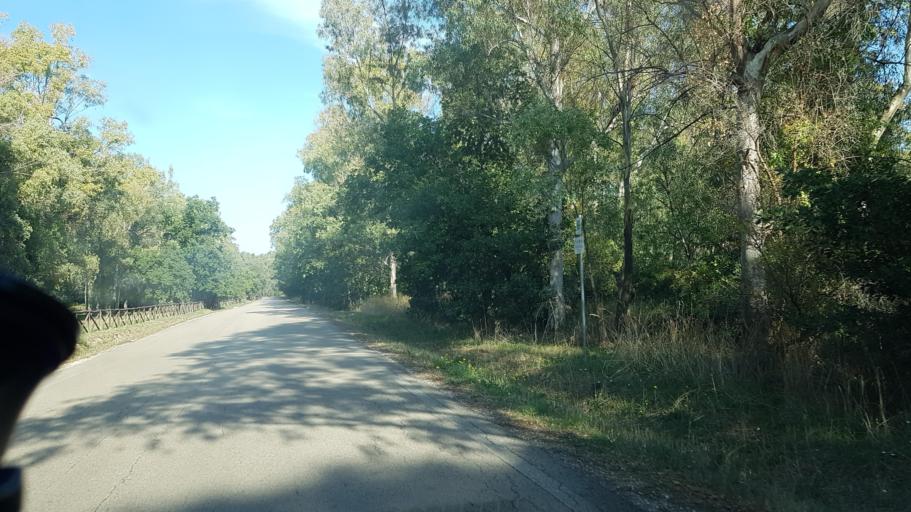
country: IT
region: Apulia
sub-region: Provincia di Foggia
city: Carapelle
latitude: 41.3859
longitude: 15.6453
